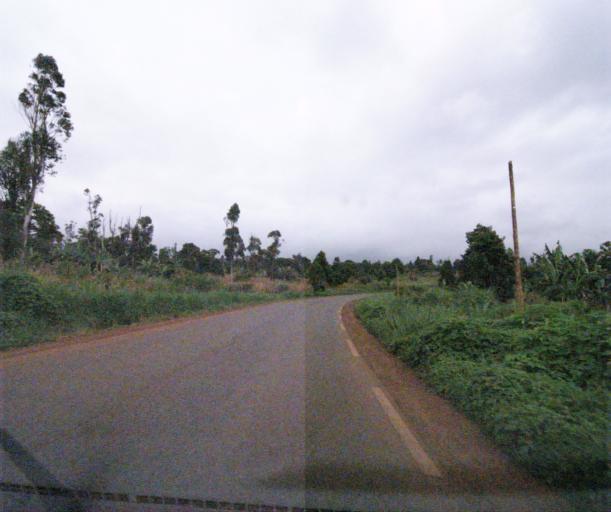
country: CM
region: West
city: Bansoa
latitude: 5.4923
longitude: 10.2207
